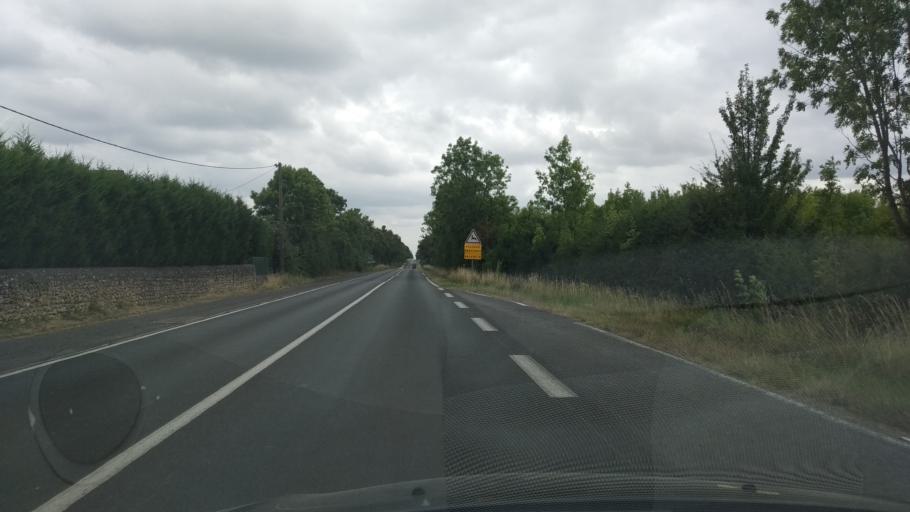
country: FR
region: Poitou-Charentes
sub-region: Departement de la Vienne
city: Smarves
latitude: 46.5014
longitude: 0.3633
